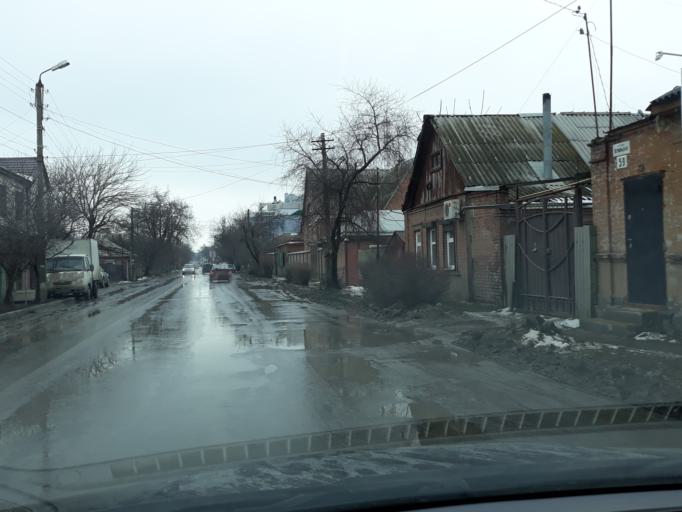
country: RU
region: Rostov
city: Taganrog
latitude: 47.2214
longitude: 38.9098
